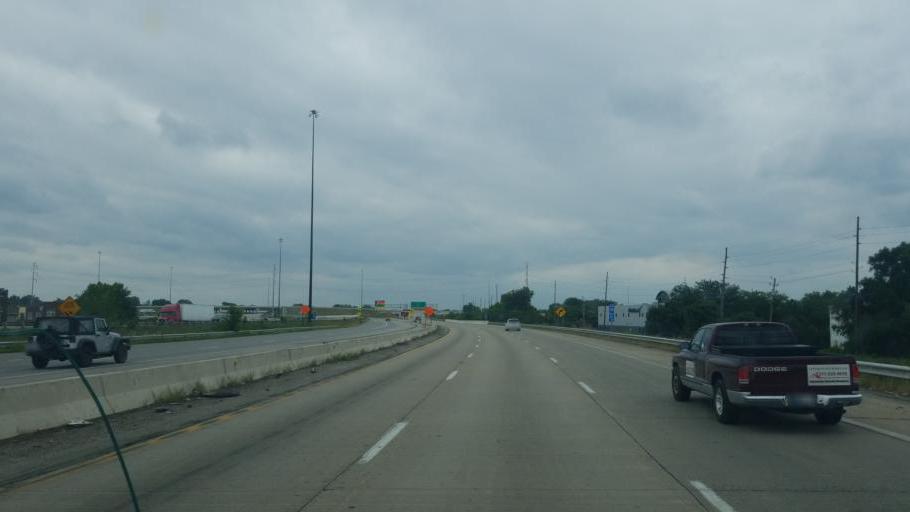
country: US
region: Indiana
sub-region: Marion County
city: Indianapolis
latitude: 39.7783
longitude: -86.1408
